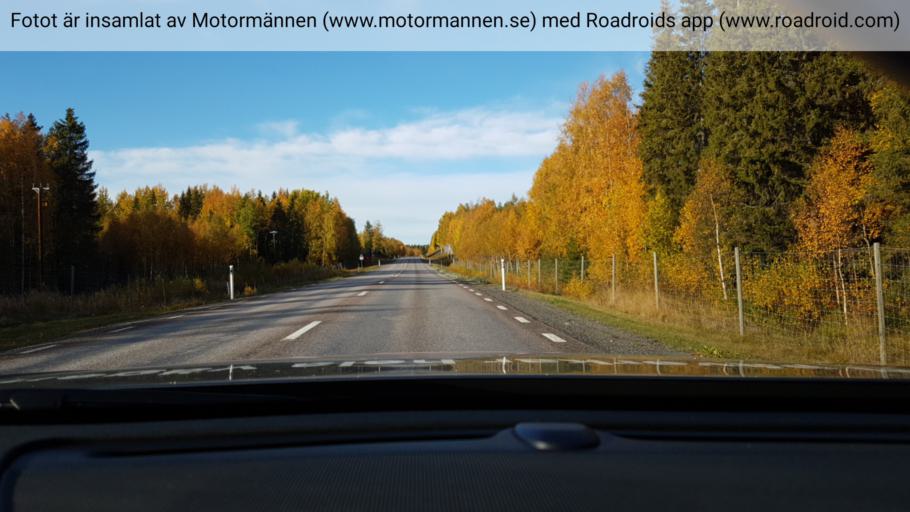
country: SE
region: Norrbotten
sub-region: Haparanda Kommun
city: Haparanda
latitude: 65.8432
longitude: 23.6806
